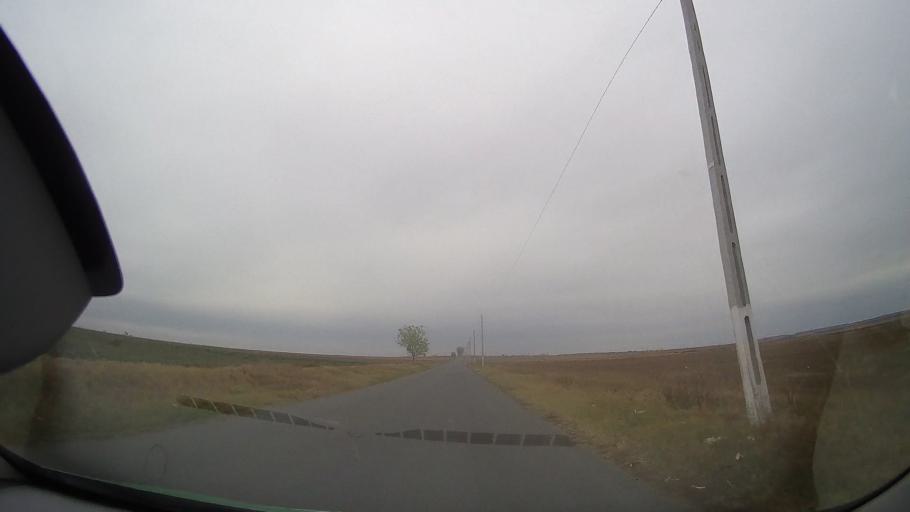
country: RO
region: Braila
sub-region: Comuna Budesti
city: Tataru
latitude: 44.8569
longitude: 27.4232
